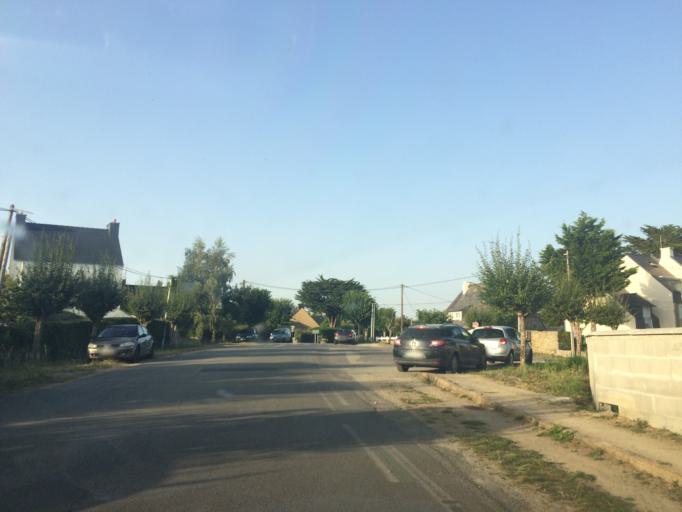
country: FR
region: Brittany
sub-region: Departement du Morbihan
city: Damgan
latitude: 47.5150
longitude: -2.5538
